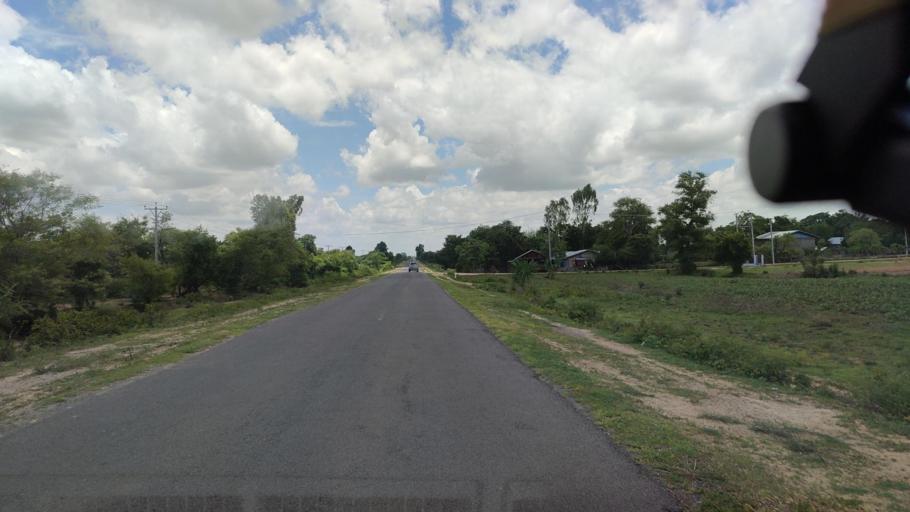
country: MM
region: Magway
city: Taungdwingyi
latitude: 20.1694
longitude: 95.4888
